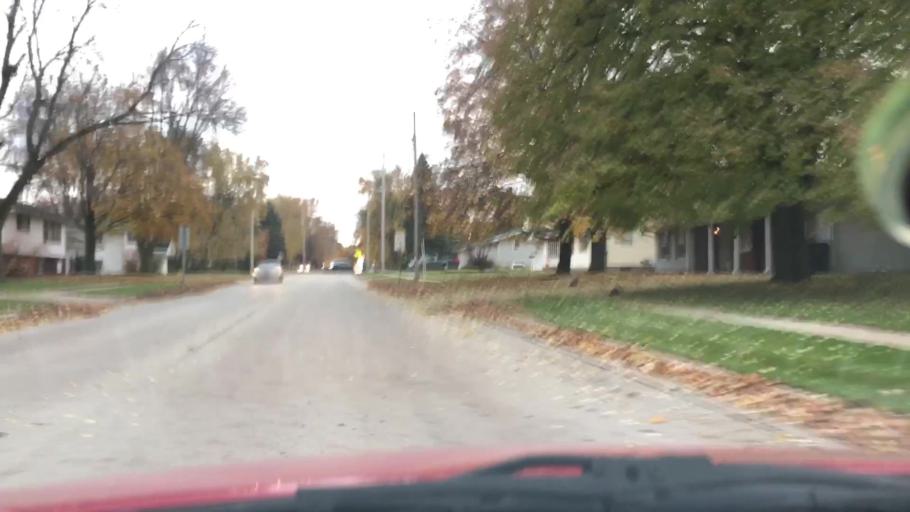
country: US
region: Wisconsin
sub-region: Outagamie County
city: Seymour
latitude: 44.5039
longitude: -88.3319
